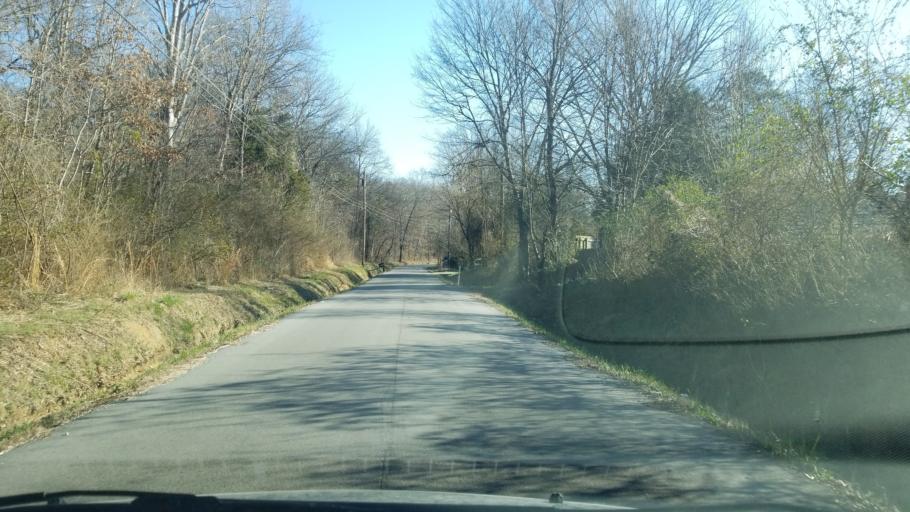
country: US
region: Tennessee
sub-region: Hamilton County
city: Collegedale
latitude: 35.0787
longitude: -85.0883
